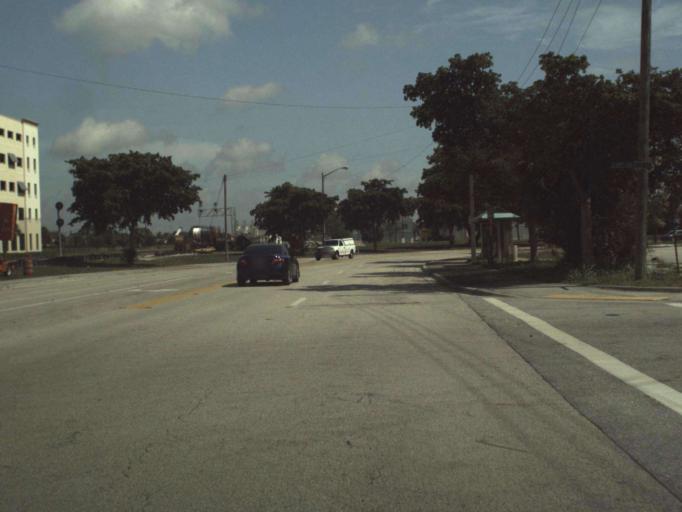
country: US
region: Florida
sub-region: Palm Beach County
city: West Palm Beach
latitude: 26.7170
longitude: -80.0550
